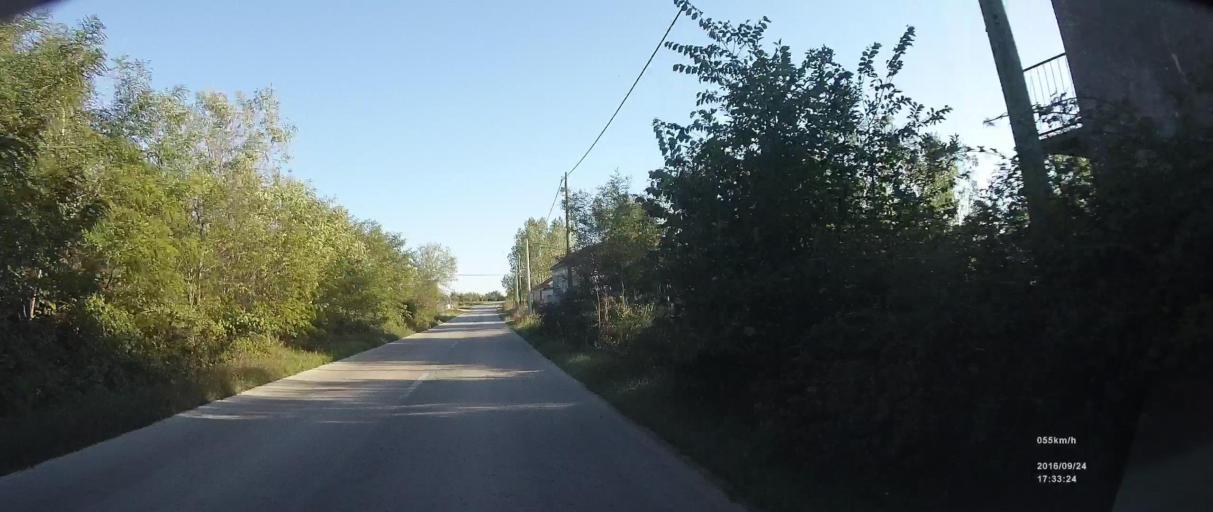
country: HR
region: Zadarska
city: Posedarje
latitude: 44.1747
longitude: 15.4568
